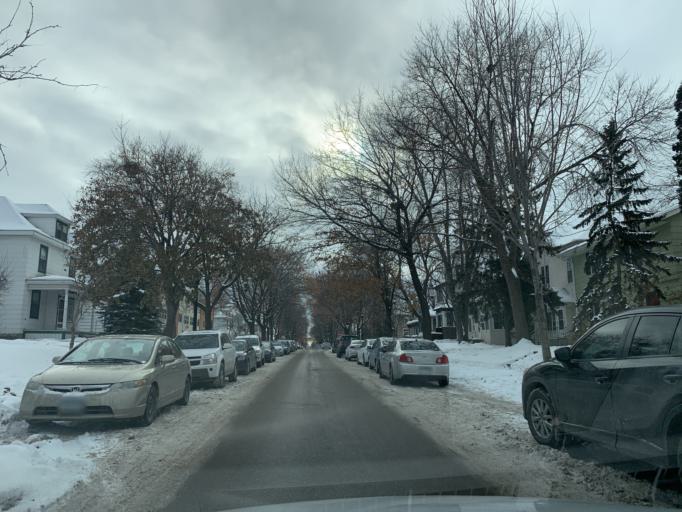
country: US
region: Minnesota
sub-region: Hennepin County
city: Minneapolis
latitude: 44.9547
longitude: -93.2945
